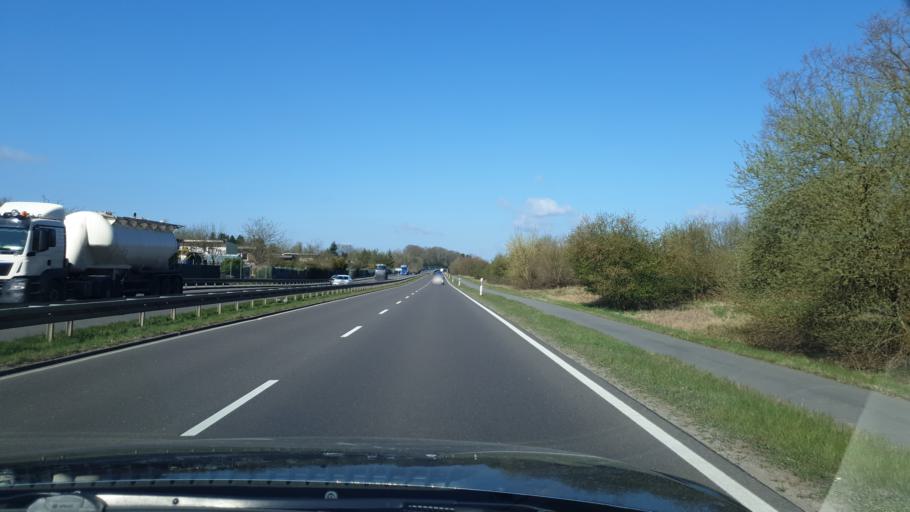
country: DE
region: Mecklenburg-Vorpommern
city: Neumuehle
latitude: 53.6183
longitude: 11.3747
